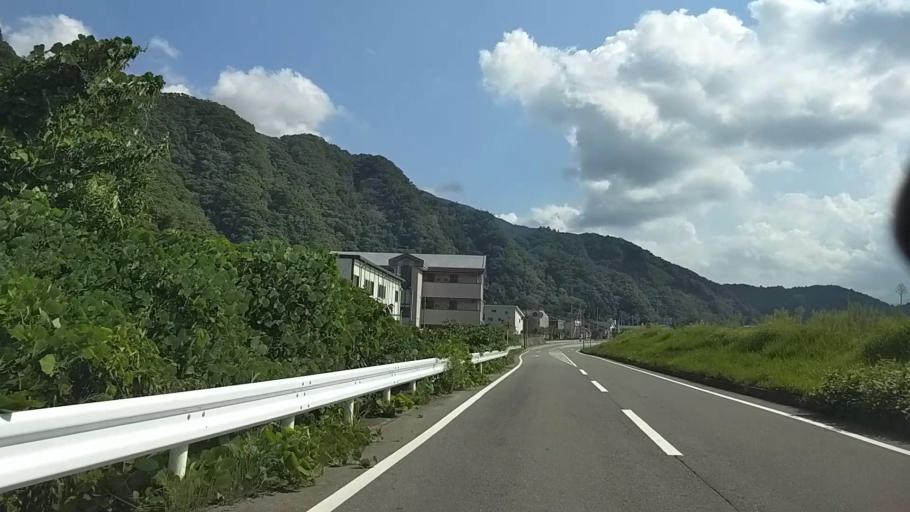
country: JP
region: Shizuoka
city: Fujinomiya
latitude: 35.3712
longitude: 138.4535
